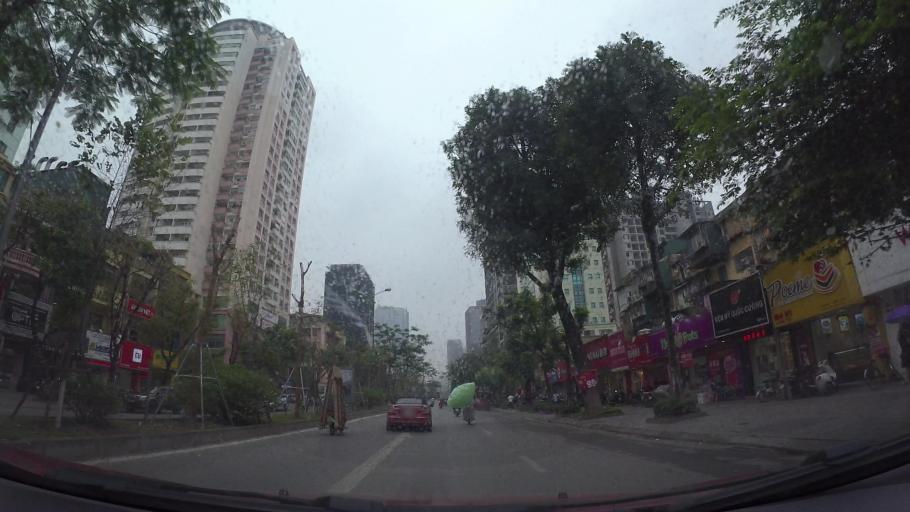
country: VN
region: Ha Noi
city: Dong Da
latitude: 21.0201
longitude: 105.8172
